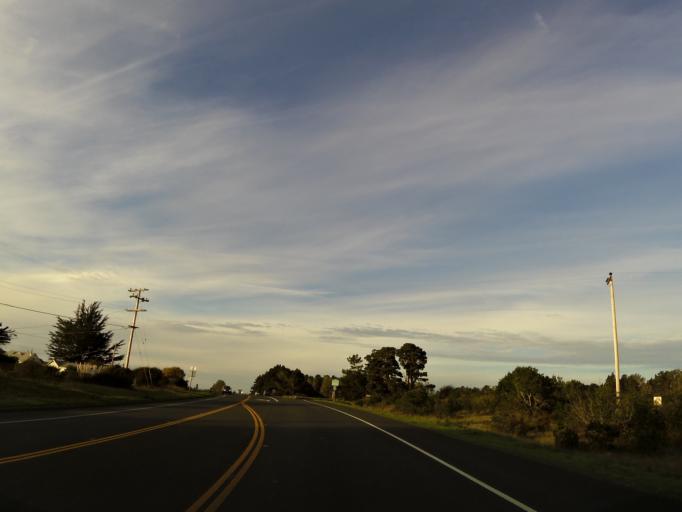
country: US
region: California
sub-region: Mendocino County
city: Fort Bragg
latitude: 39.3639
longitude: -123.8089
